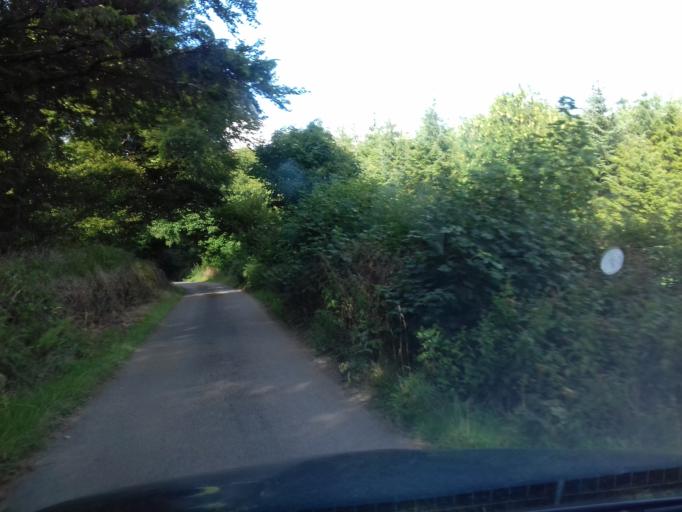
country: IE
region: Leinster
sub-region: Kilkenny
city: Graiguenamanagh
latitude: 52.5638
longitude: -7.0051
